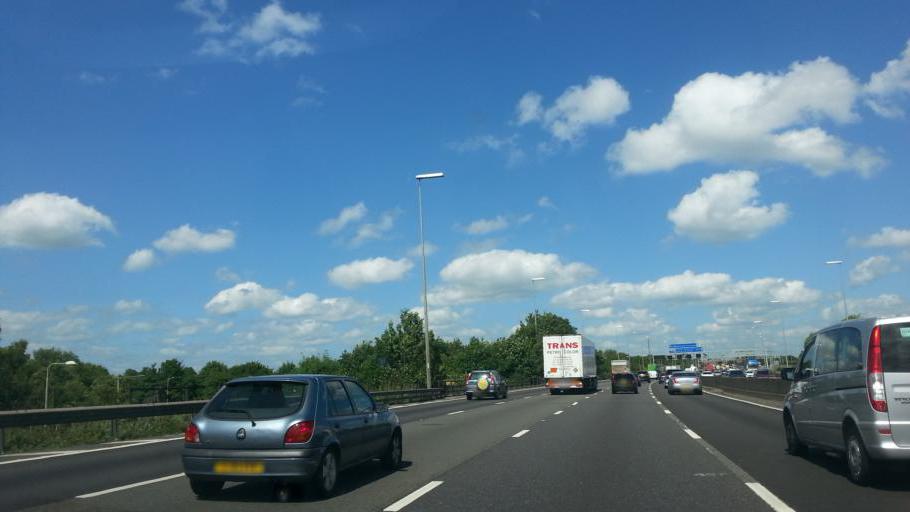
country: GB
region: England
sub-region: Hertfordshire
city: Chorleywood
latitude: 51.6364
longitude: -0.5121
